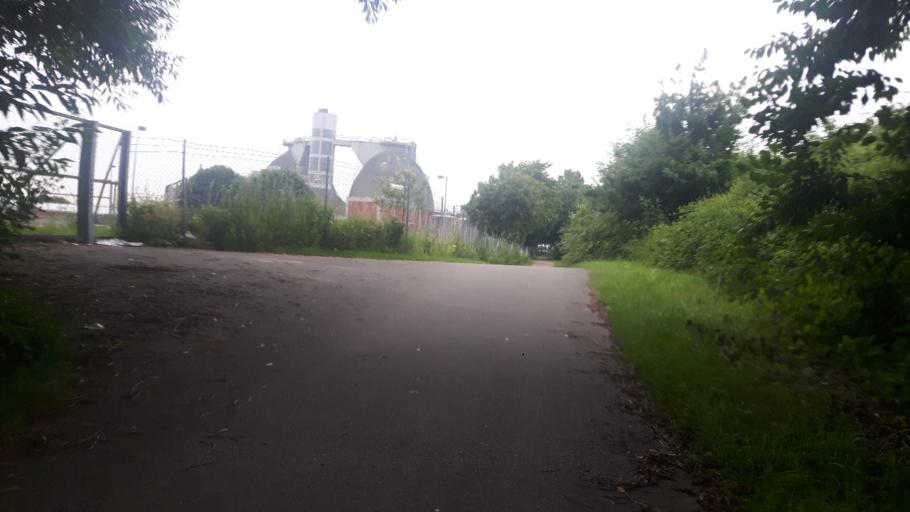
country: DE
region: Schleswig-Holstein
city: Bad Schwartau
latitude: 53.9013
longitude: 10.6929
